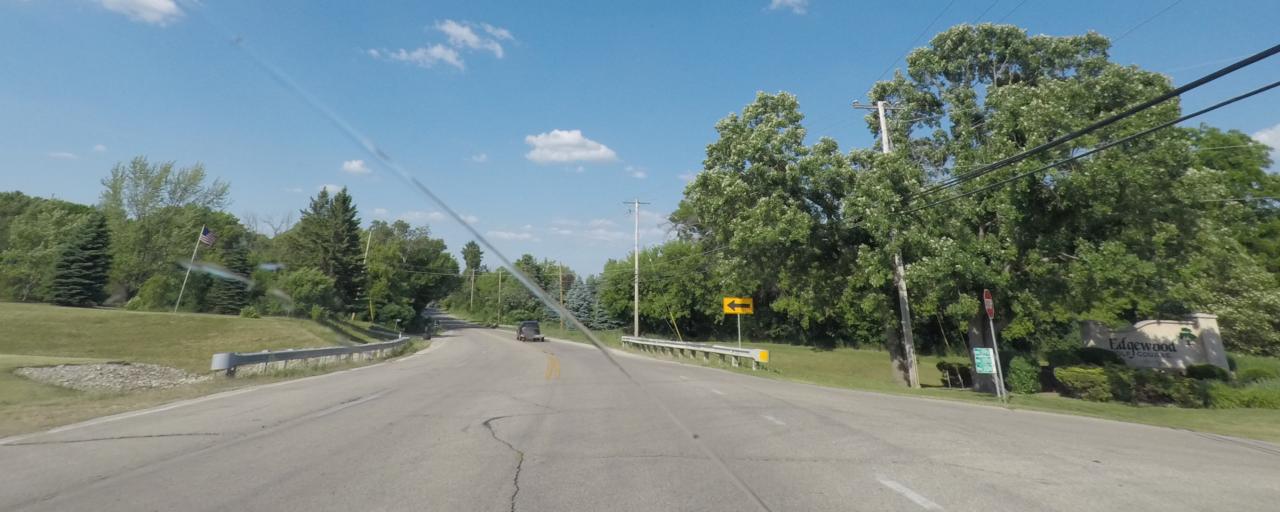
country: US
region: Wisconsin
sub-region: Waukesha County
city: Big Bend
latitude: 42.8640
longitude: -88.2292
